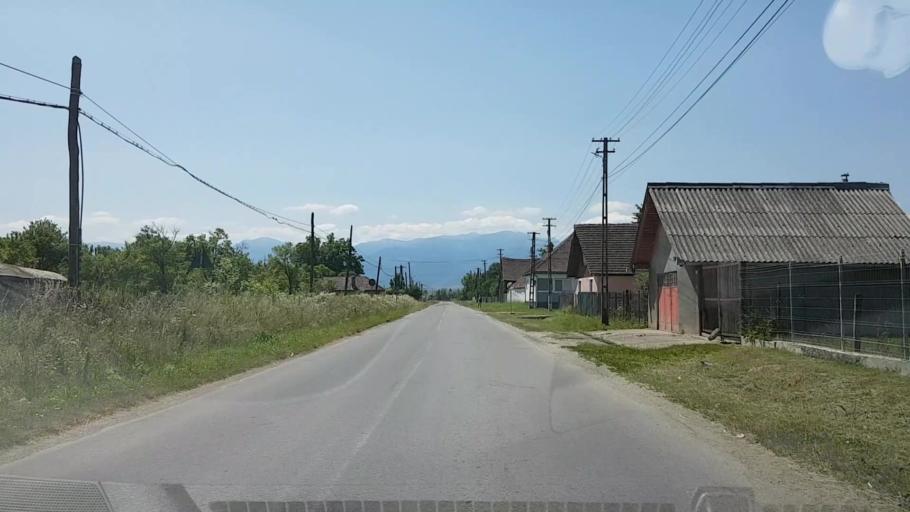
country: RO
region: Brasov
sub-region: Comuna Voila
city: Voila
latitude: 45.8355
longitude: 24.8325
